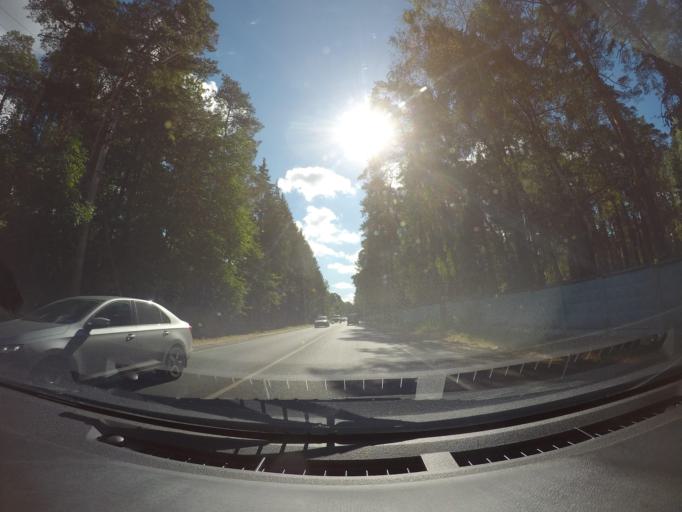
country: RU
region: Moskovskaya
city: Kratovo
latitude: 55.5981
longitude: 38.1790
